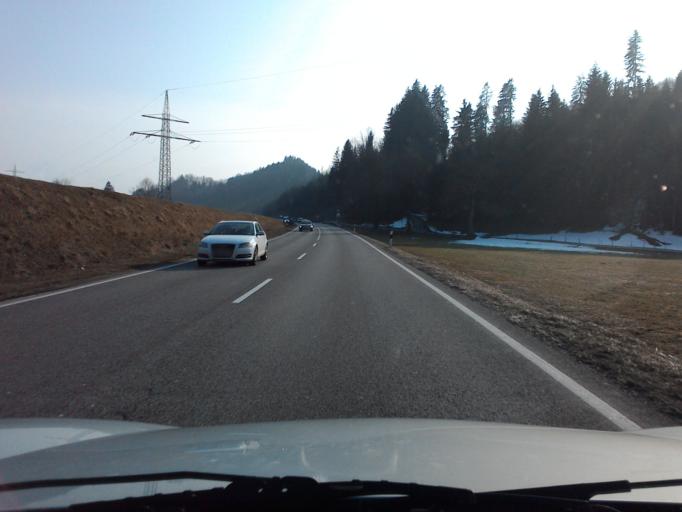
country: DE
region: Bavaria
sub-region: Swabia
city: Sonthofen
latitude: 47.5017
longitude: 10.2671
